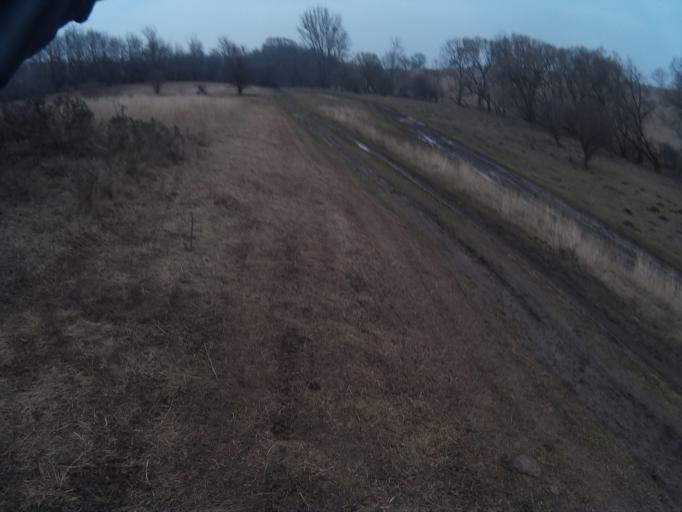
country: HU
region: Fejer
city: Many
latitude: 47.5420
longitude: 18.5802
